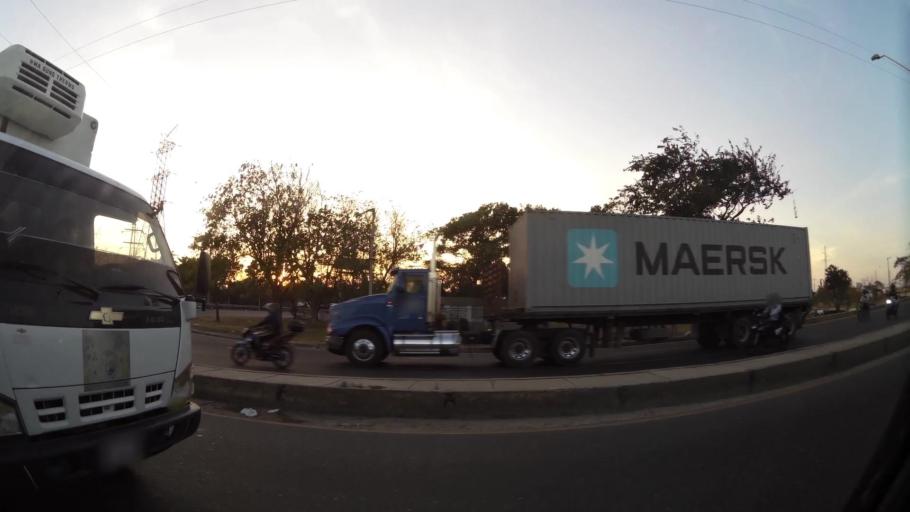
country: CO
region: Atlantico
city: Soledad
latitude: 10.9335
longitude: -74.7801
